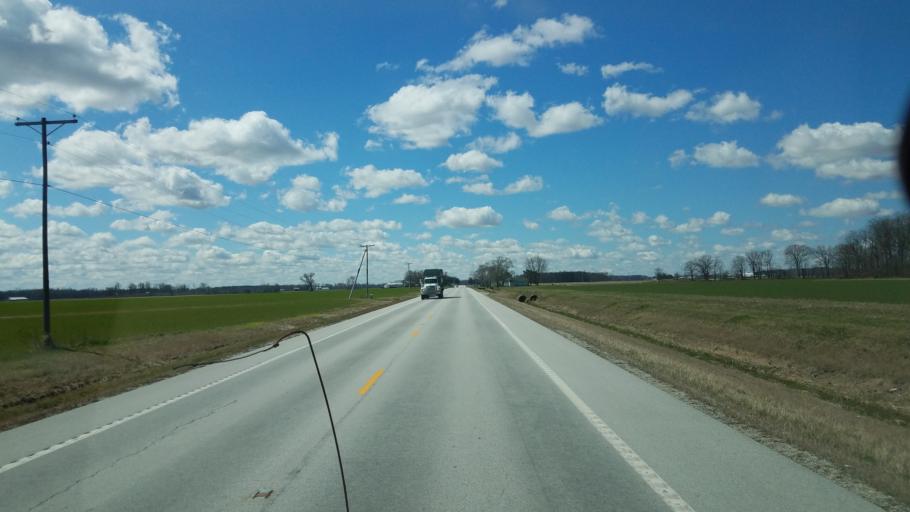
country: US
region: Ohio
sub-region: Sandusky County
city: Ballville
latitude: 41.2888
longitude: -83.1780
